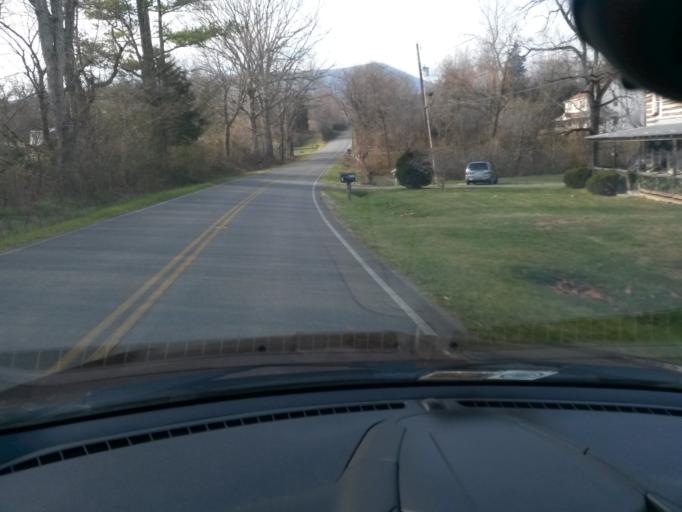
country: US
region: Virginia
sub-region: Botetourt County
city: Daleville
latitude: 37.4519
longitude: -79.9599
